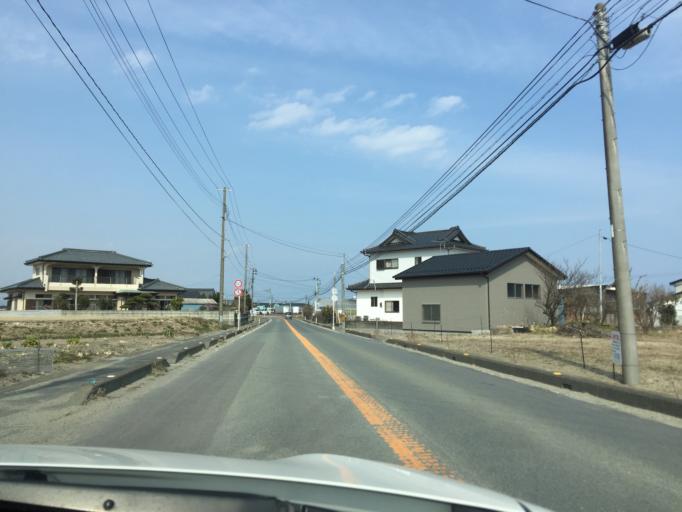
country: JP
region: Fukushima
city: Iwaki
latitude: 37.0111
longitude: 140.9685
